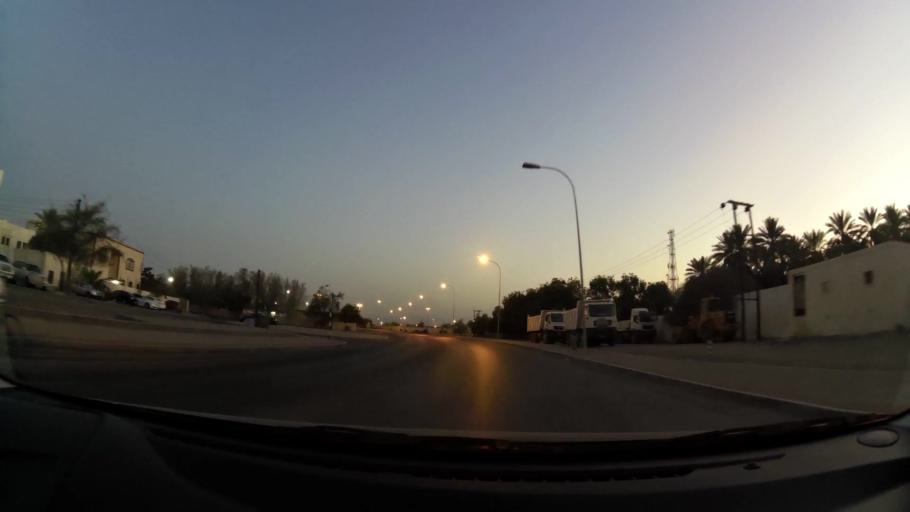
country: OM
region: Muhafazat Masqat
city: As Sib al Jadidah
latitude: 23.6674
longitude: 58.1840
